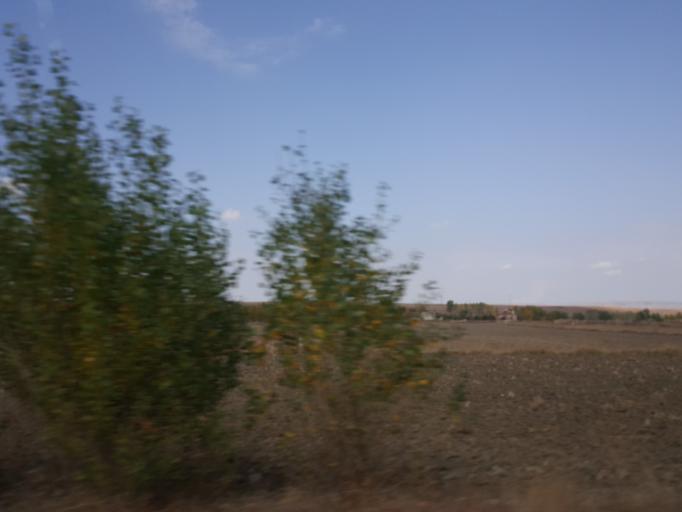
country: TR
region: Corum
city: Alaca
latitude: 40.1406
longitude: 34.8217
